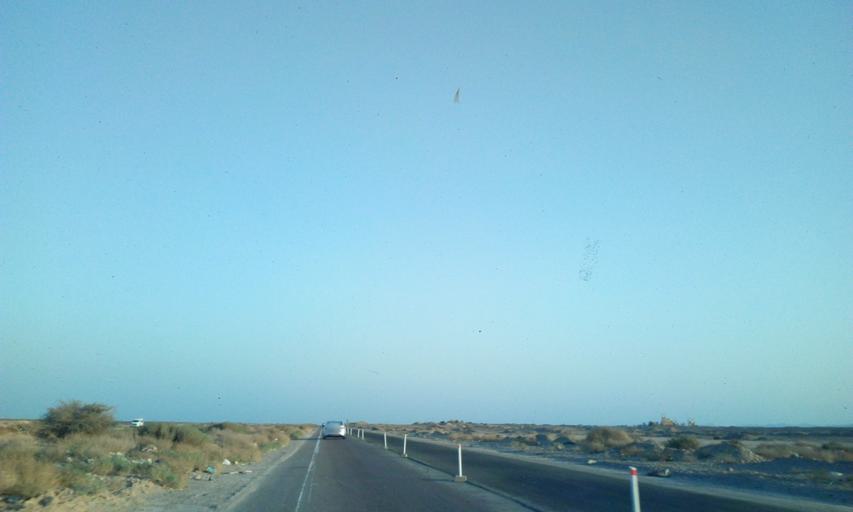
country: EG
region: South Sinai
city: Tor
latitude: 27.9021
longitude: 33.4009
